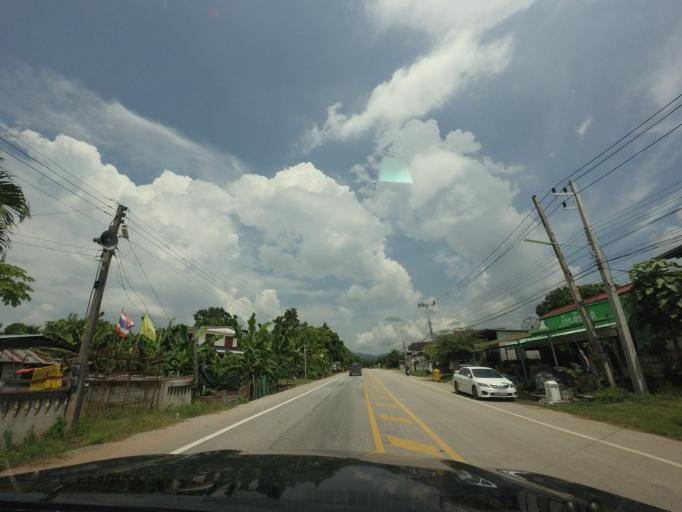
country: TH
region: Khon Kaen
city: Wiang Kao
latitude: 16.6747
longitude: 102.2968
